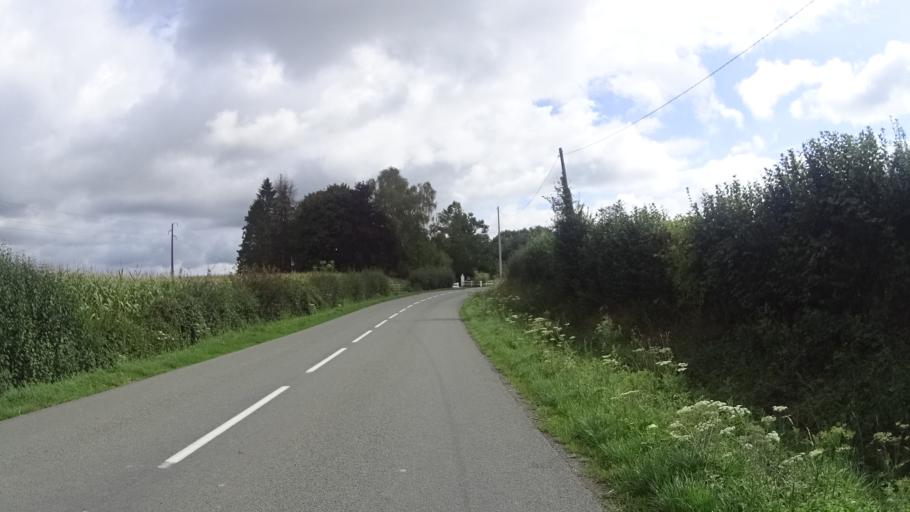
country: FR
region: Nord-Pas-de-Calais
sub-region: Departement du Nord
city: Landrecies
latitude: 50.0999
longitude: 3.6458
